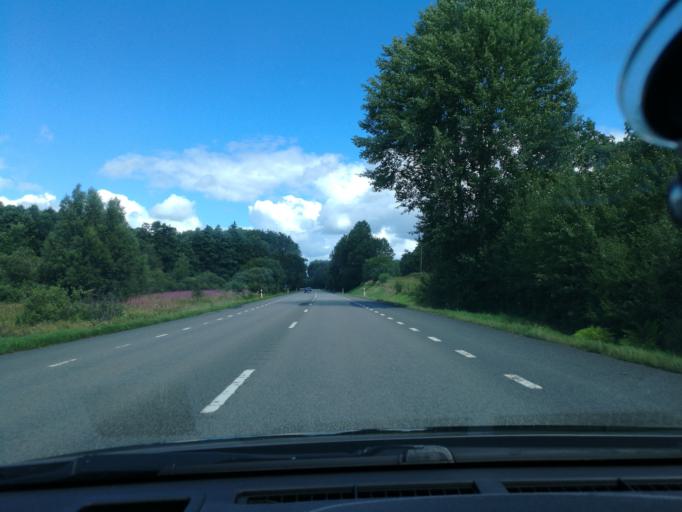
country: SE
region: Skane
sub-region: Hassleholms Kommun
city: Tormestorp
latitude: 56.0988
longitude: 13.7763
